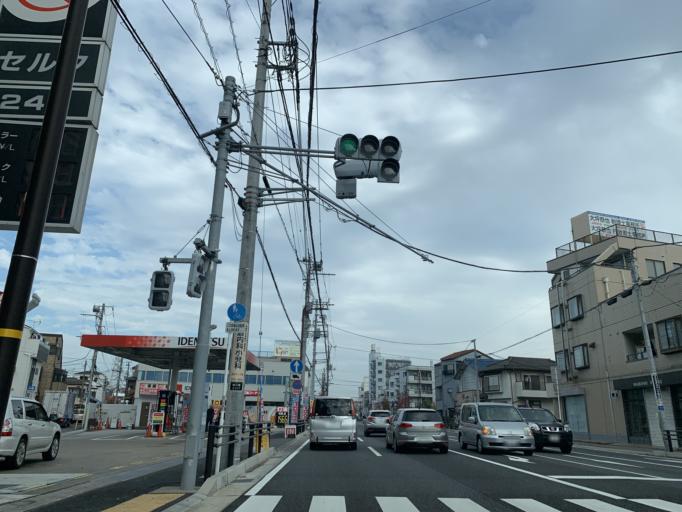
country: JP
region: Tokyo
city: Urayasu
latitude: 35.7134
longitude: 139.9283
